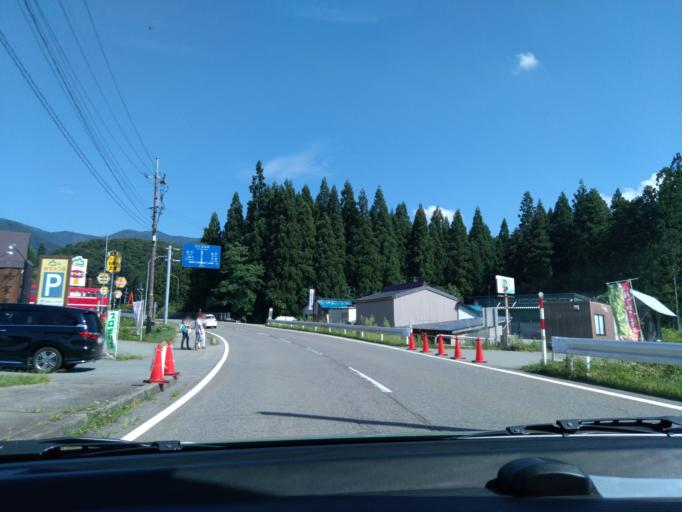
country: JP
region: Akita
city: Kakunodatemachi
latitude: 39.7399
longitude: 140.7142
